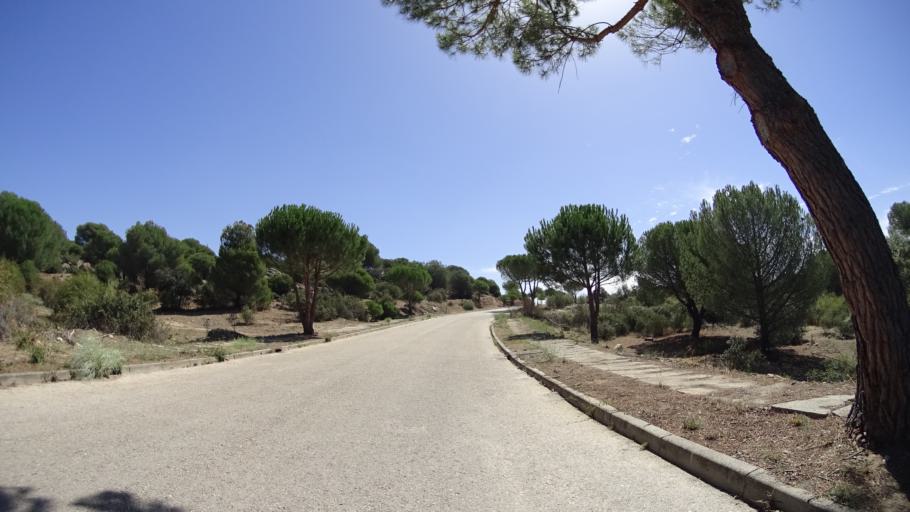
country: ES
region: Madrid
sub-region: Provincia de Madrid
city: Torrelodones
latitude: 40.5704
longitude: -3.9412
